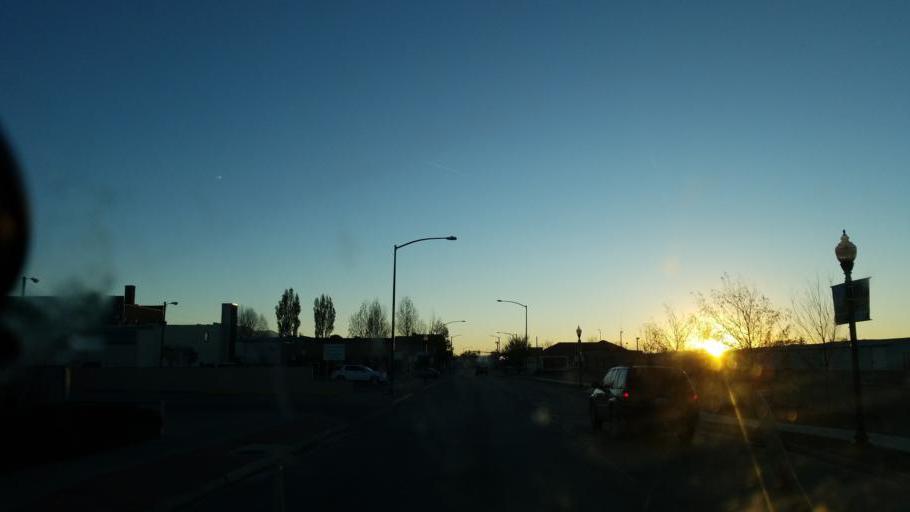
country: US
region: Colorado
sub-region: Alamosa County
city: Alamosa
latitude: 37.4671
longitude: -105.8682
